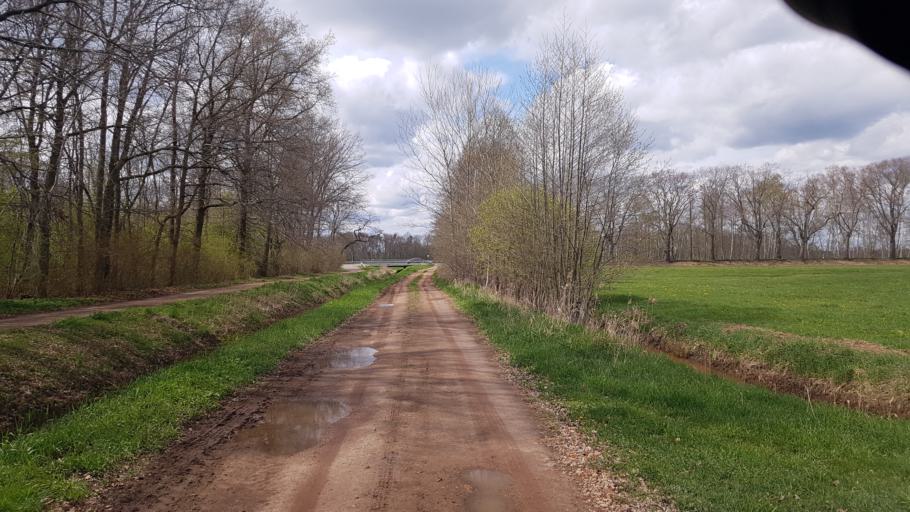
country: DE
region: Brandenburg
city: Bronkow
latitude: 51.6186
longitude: 13.9222
